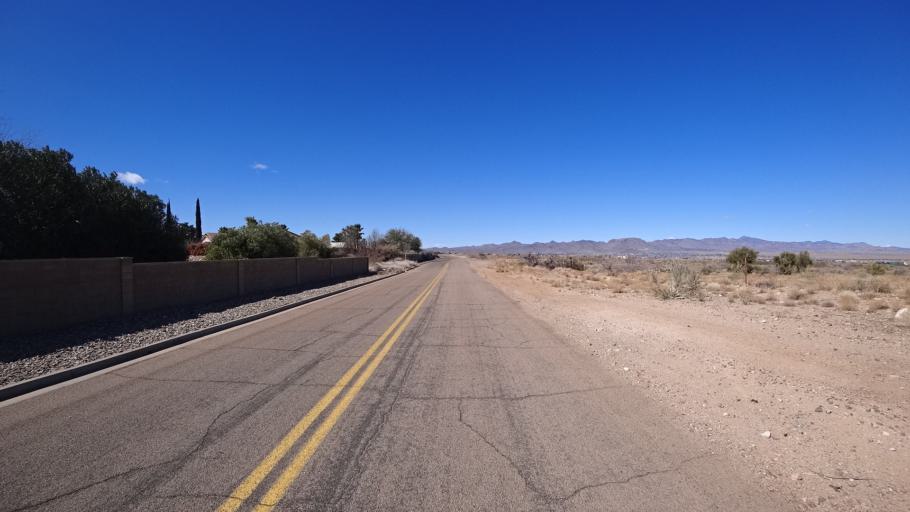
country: US
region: Arizona
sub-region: Mohave County
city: Kingman
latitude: 35.2040
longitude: -113.9603
